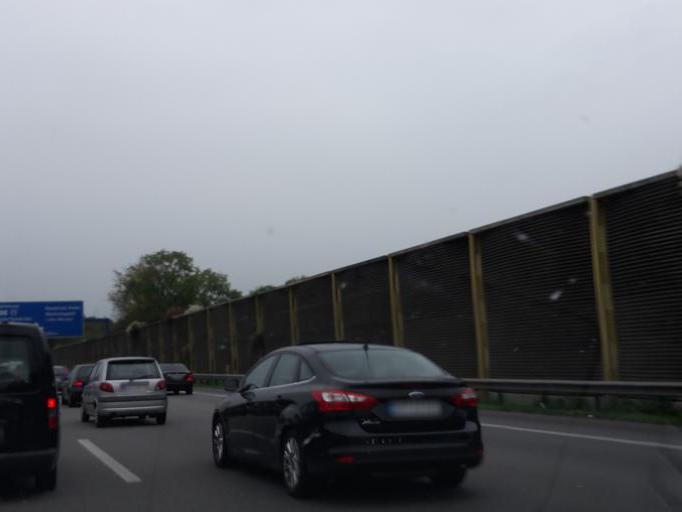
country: DE
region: North Rhine-Westphalia
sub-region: Regierungsbezirk Munster
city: Lotte
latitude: 52.3093
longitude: 7.9481
